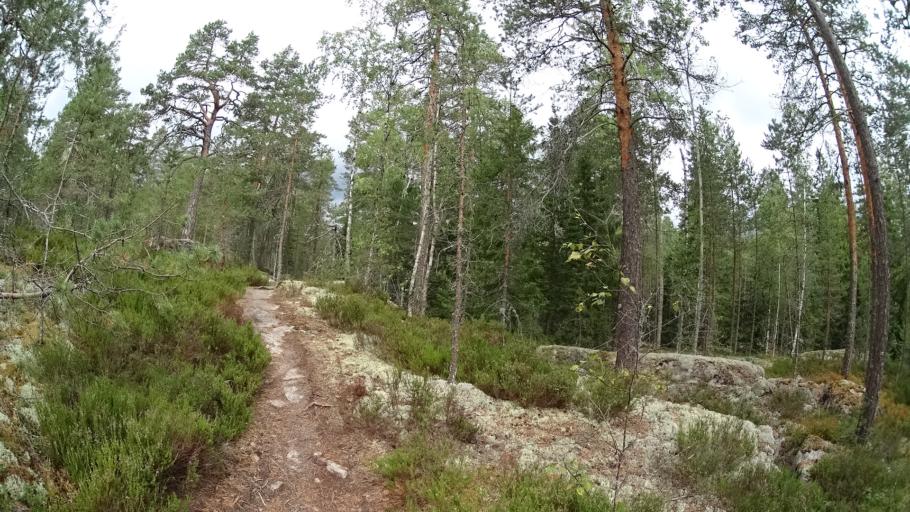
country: FI
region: Uusimaa
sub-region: Helsinki
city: Espoo
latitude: 60.3043
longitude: 24.5809
